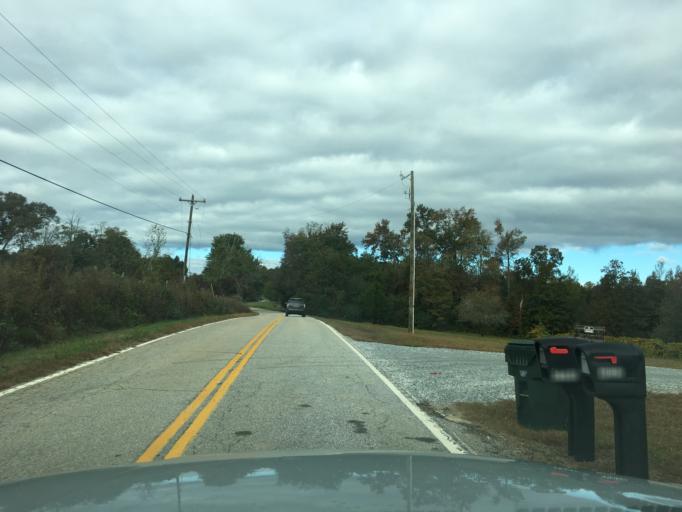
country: US
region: South Carolina
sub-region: Greenville County
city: Tigerville
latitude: 35.0586
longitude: -82.2619
